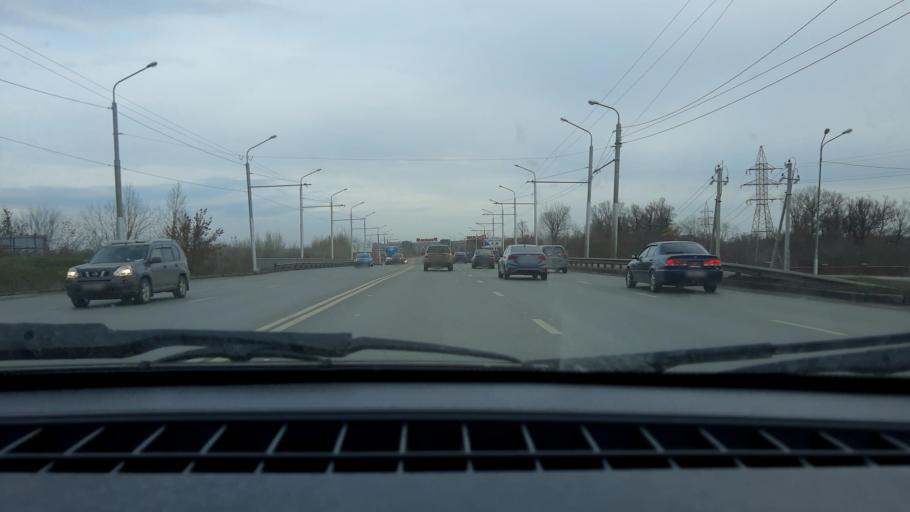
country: RU
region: Bashkortostan
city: Ufa
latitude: 54.7847
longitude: 56.0756
